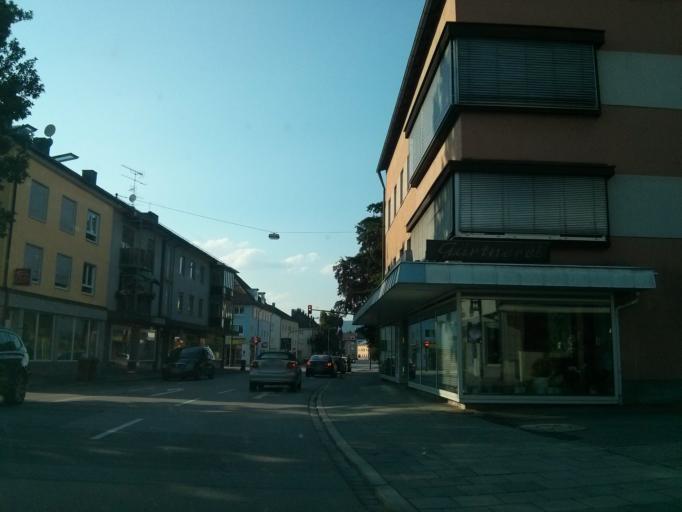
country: DE
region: Bavaria
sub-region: Lower Bavaria
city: Deggendorf
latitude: 48.8366
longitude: 12.9614
